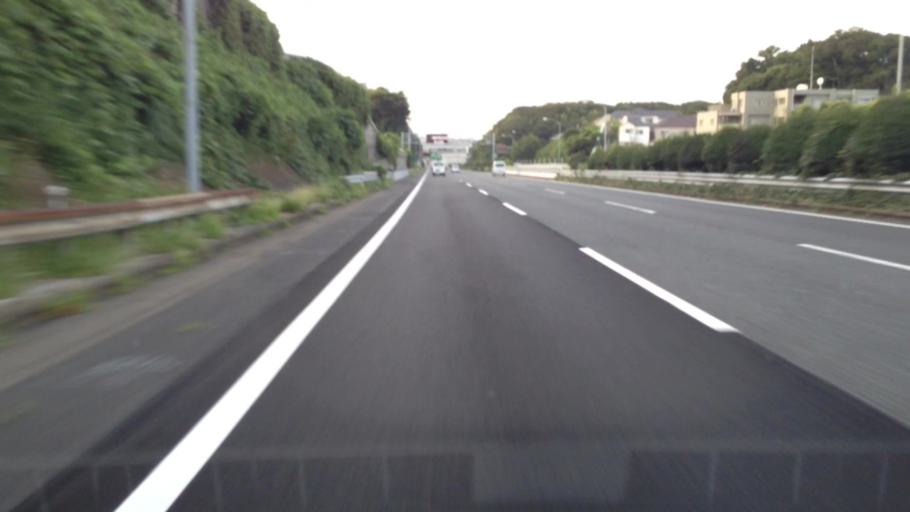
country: JP
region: Kanagawa
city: Yokohama
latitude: 35.5076
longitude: 139.5927
